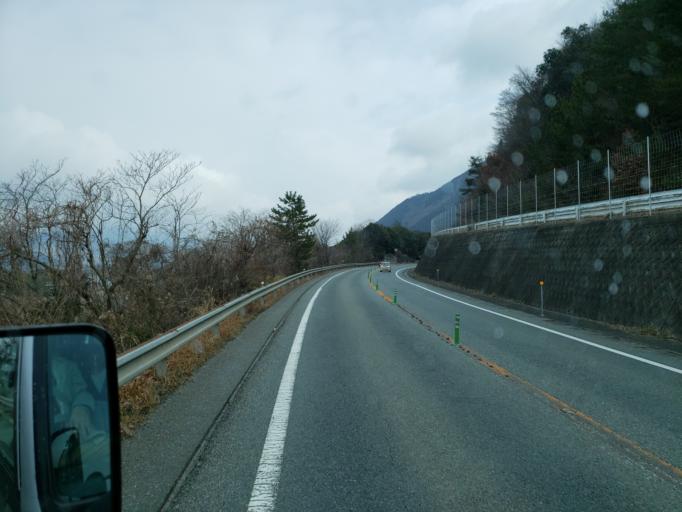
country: JP
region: Hyogo
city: Nishiwaki
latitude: 35.0315
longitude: 134.7661
